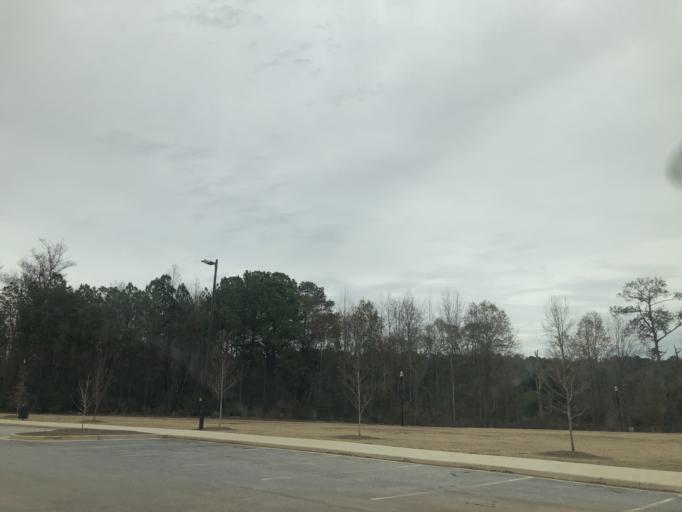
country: US
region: Georgia
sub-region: Clayton County
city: Conley
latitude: 33.6267
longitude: -84.2541
